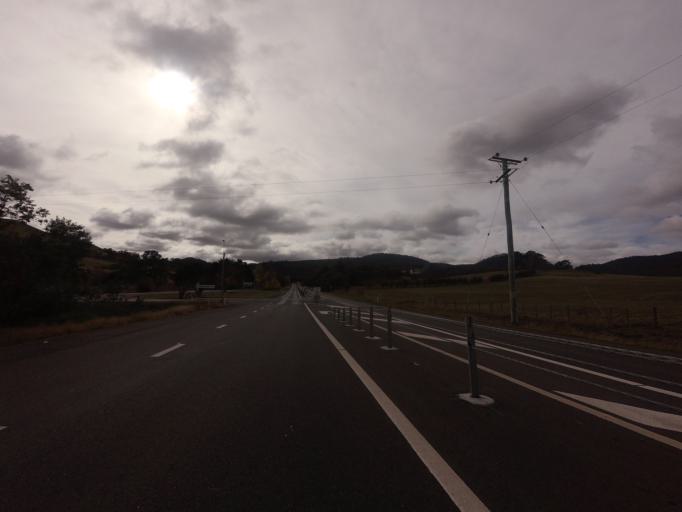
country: AU
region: Tasmania
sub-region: Brighton
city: Bridgewater
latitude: -42.5935
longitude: 147.2221
